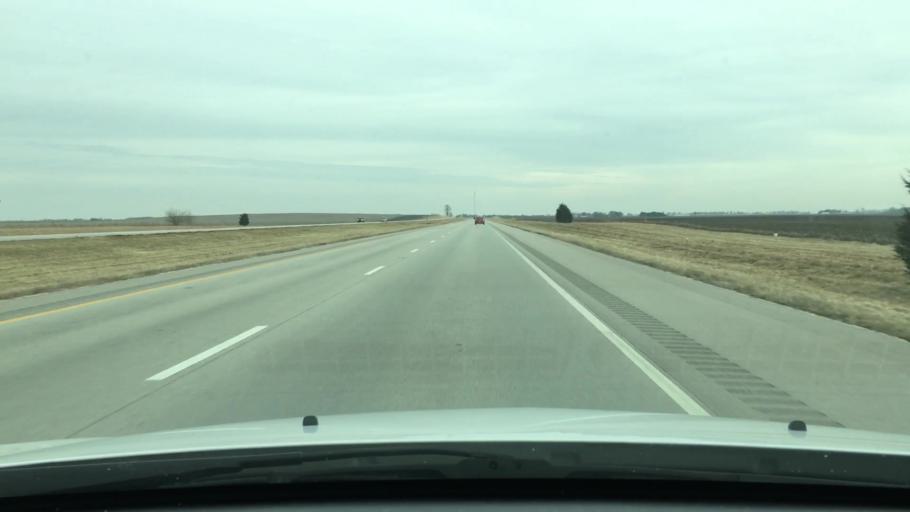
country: US
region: Illinois
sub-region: Morgan County
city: Jacksonville
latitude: 39.7380
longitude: -90.1103
